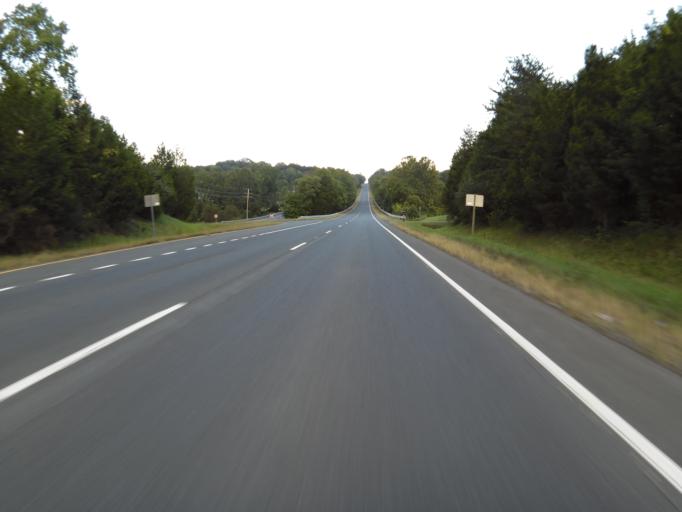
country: US
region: Virginia
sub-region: Fauquier County
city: Warrenton
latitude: 38.7100
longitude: -77.8472
